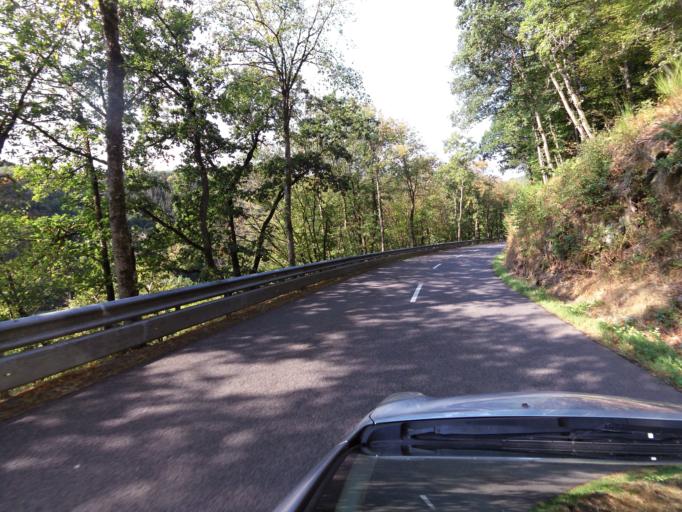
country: LU
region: Diekirch
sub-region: Canton de Diekirch
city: Bourscheid
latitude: 49.9200
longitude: 6.0303
